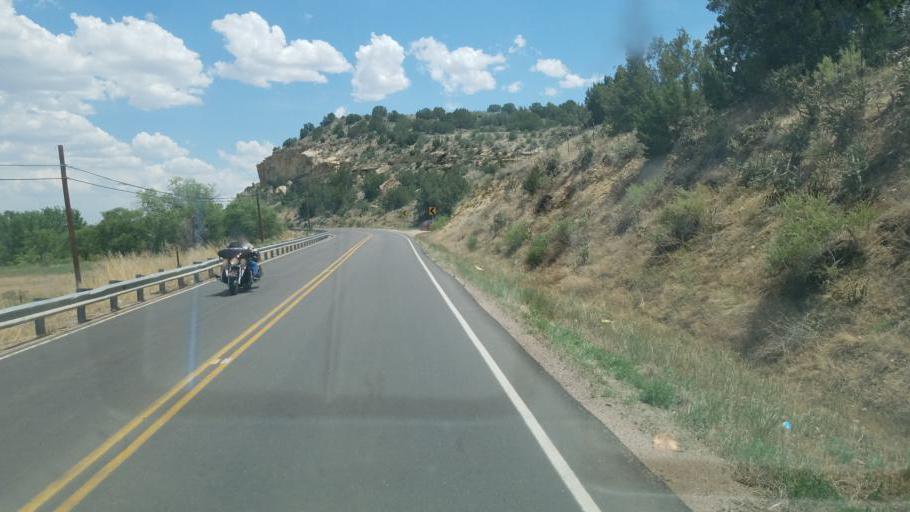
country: US
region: Colorado
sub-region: Fremont County
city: Lincoln Park
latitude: 38.4157
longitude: -105.1808
